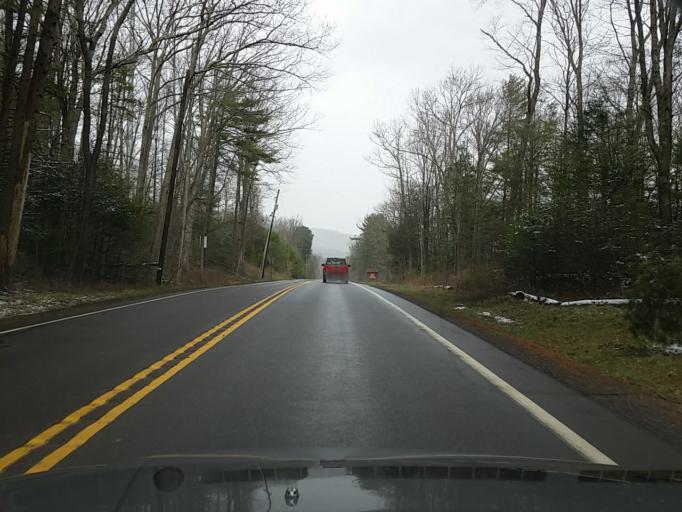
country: US
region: Pennsylvania
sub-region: Sullivan County
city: Laporte
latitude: 41.2916
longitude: -76.2944
